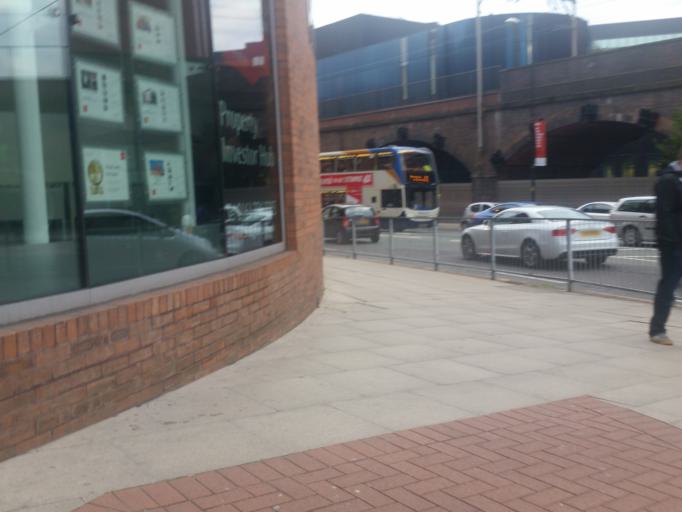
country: GB
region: England
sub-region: Manchester
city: Hulme
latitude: 53.4743
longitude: -2.2479
